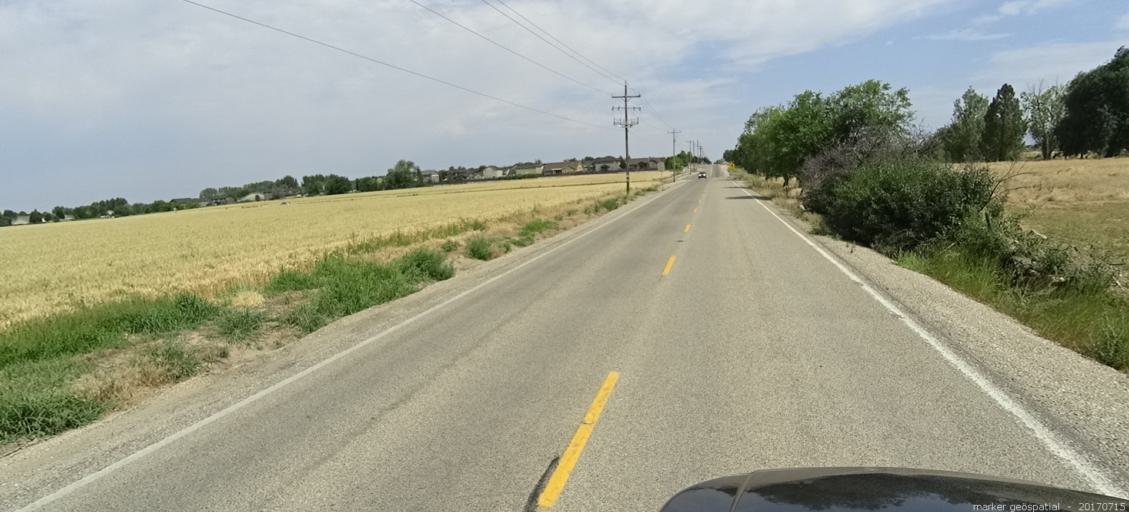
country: US
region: Idaho
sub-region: Ada County
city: Garden City
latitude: 43.5405
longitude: -116.2742
